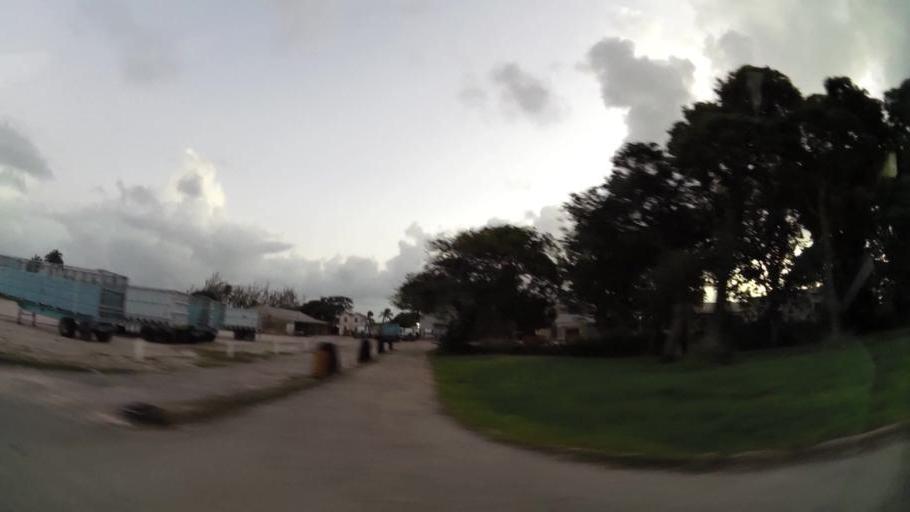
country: BB
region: Saint Philip
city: Crane
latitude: 13.1188
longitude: -59.4973
